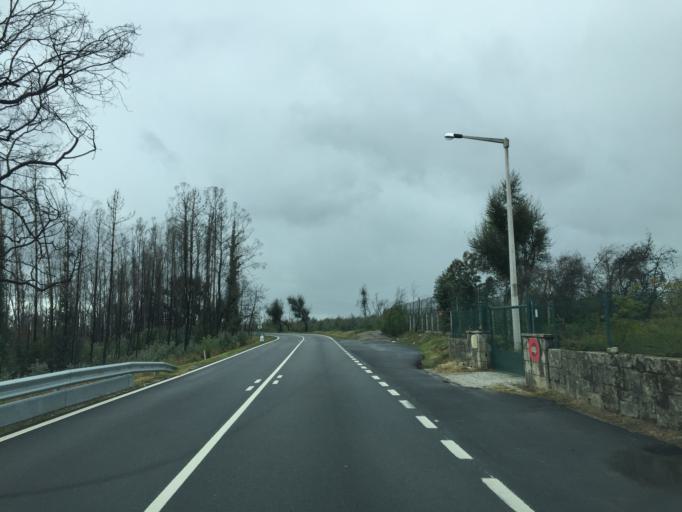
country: PT
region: Coimbra
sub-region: Tabua
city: Tabua
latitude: 40.3291
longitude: -7.9483
